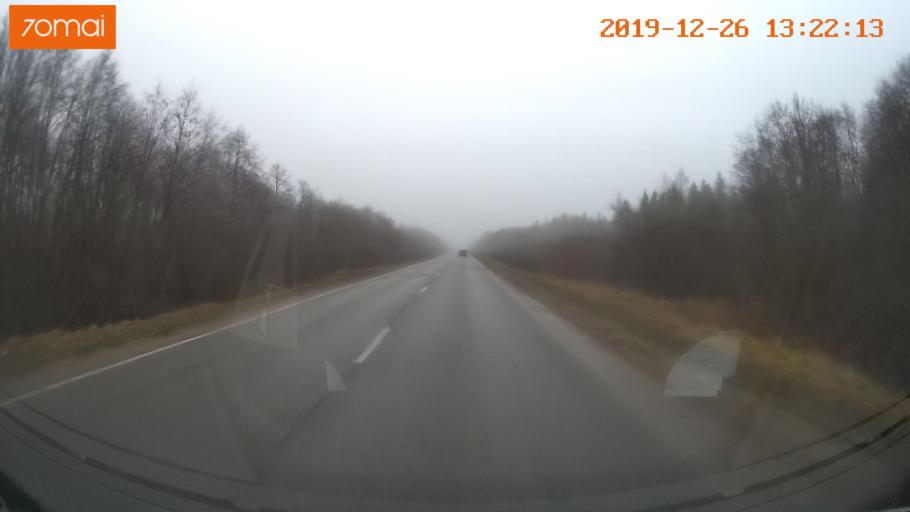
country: RU
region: Vologda
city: Cherepovets
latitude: 58.9044
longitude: 38.1690
